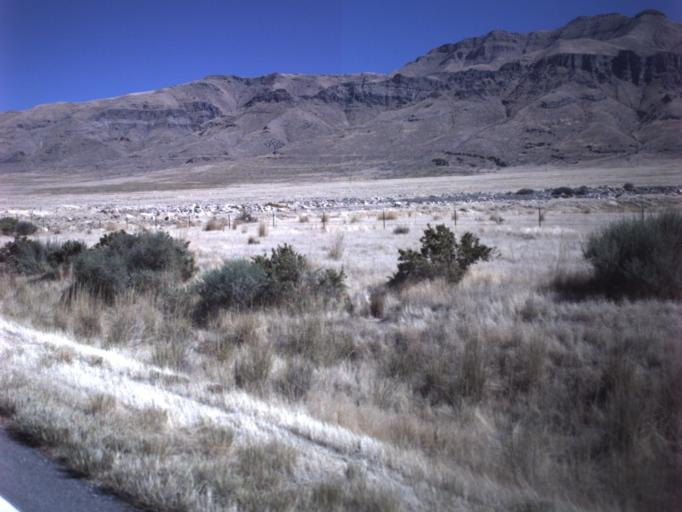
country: US
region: Utah
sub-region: Tooele County
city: Grantsville
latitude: 40.6436
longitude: -112.6882
